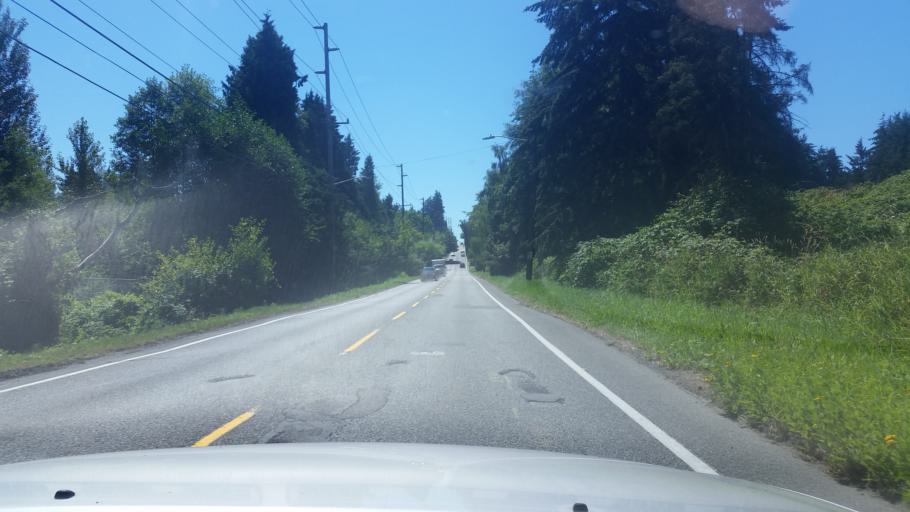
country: US
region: Washington
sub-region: King County
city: Shoreline
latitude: 47.7301
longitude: -122.3236
